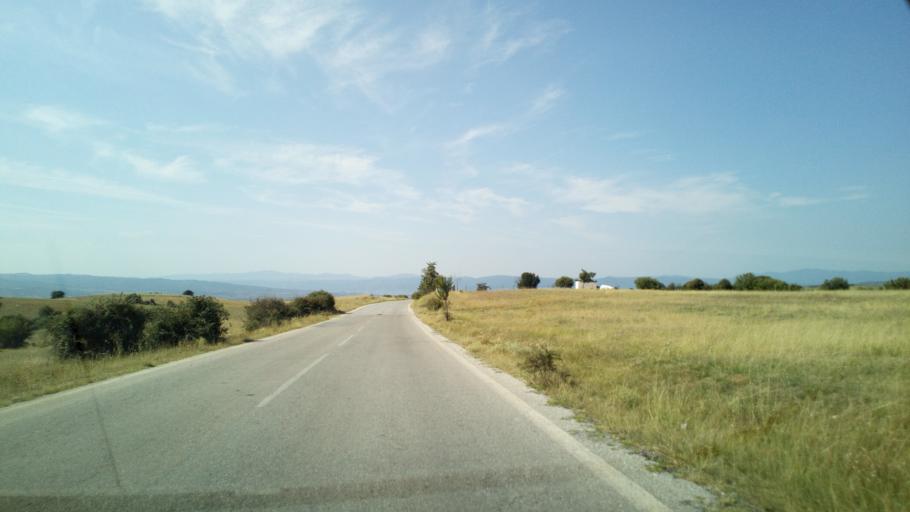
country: GR
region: Central Macedonia
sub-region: Nomos Thessalonikis
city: Nea Apollonia
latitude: 40.5112
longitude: 23.4741
